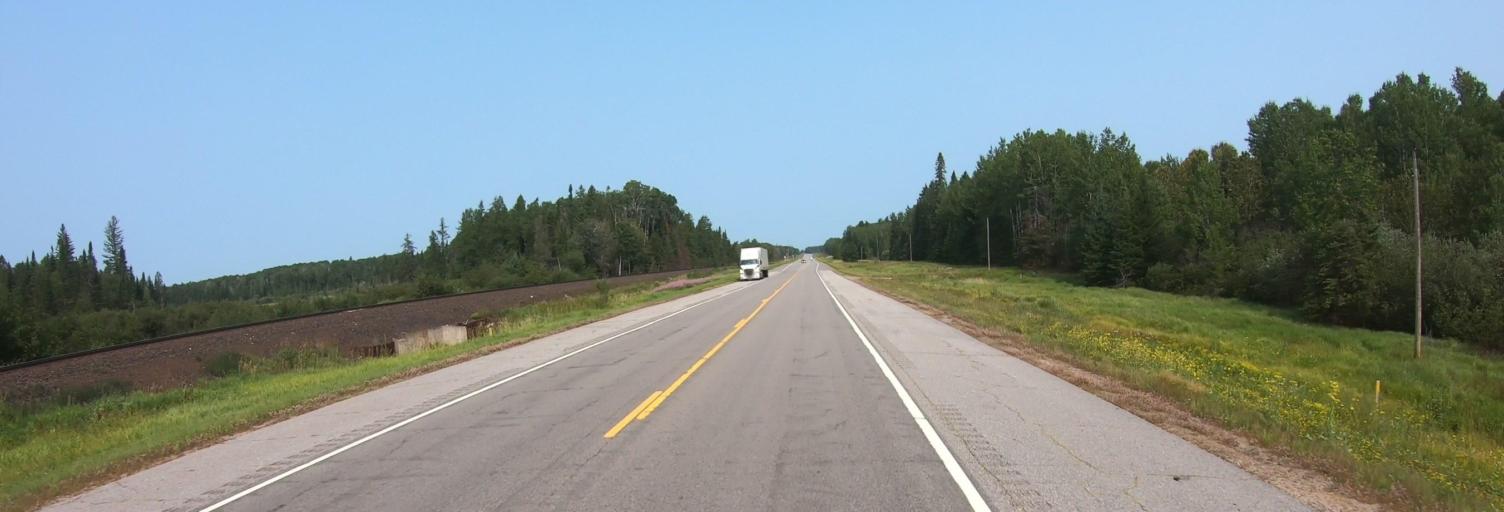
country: US
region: Minnesota
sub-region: Saint Louis County
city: Chisholm
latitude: 48.1572
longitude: -92.8705
